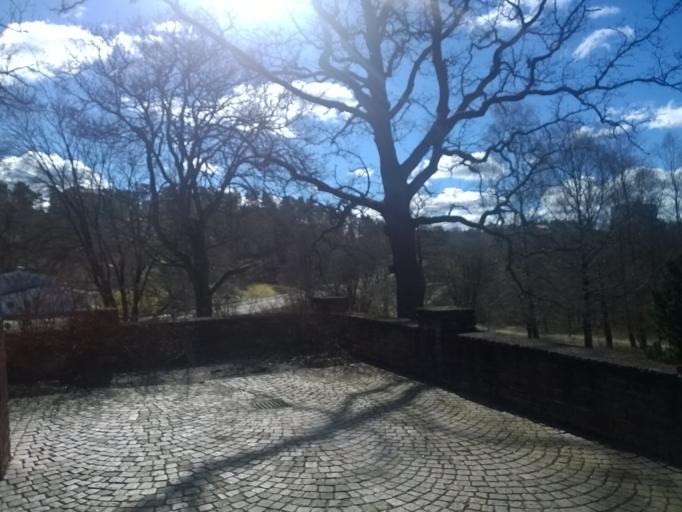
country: SE
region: Vaestra Goetaland
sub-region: Boras Kommun
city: Boras
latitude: 57.7245
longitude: 12.9085
